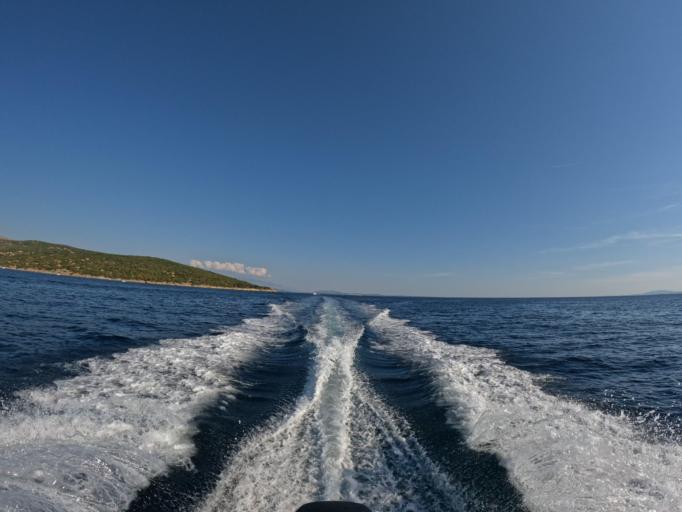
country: HR
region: Primorsko-Goranska
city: Punat
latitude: 44.9867
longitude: 14.6086
